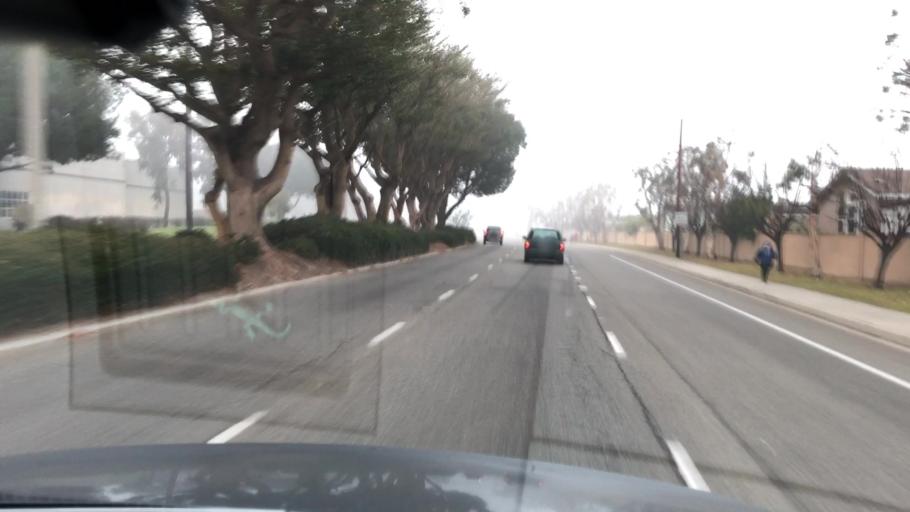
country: US
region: California
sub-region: Ventura County
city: Oxnard
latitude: 34.1808
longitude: -119.1598
